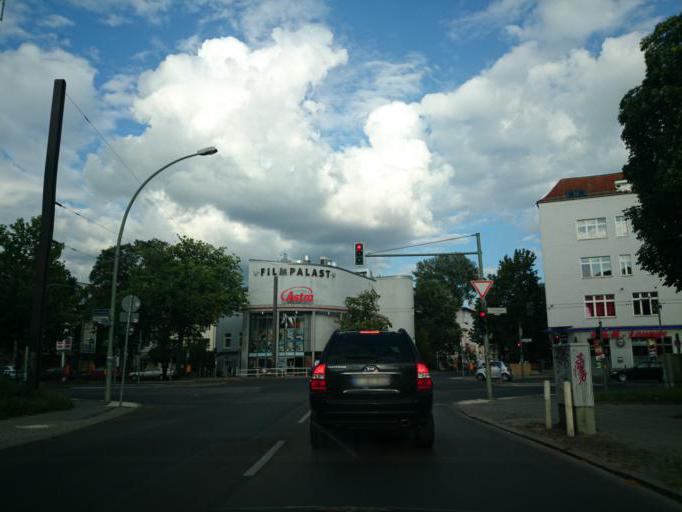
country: DE
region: Berlin
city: Johannisthal
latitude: 52.4467
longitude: 13.5060
